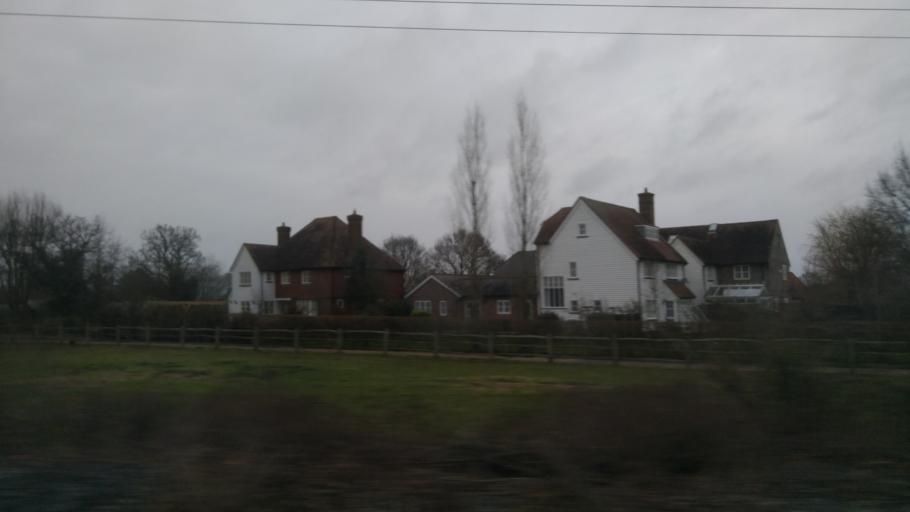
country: GB
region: England
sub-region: Kent
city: Staplehurst
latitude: 51.1708
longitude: 0.5611
